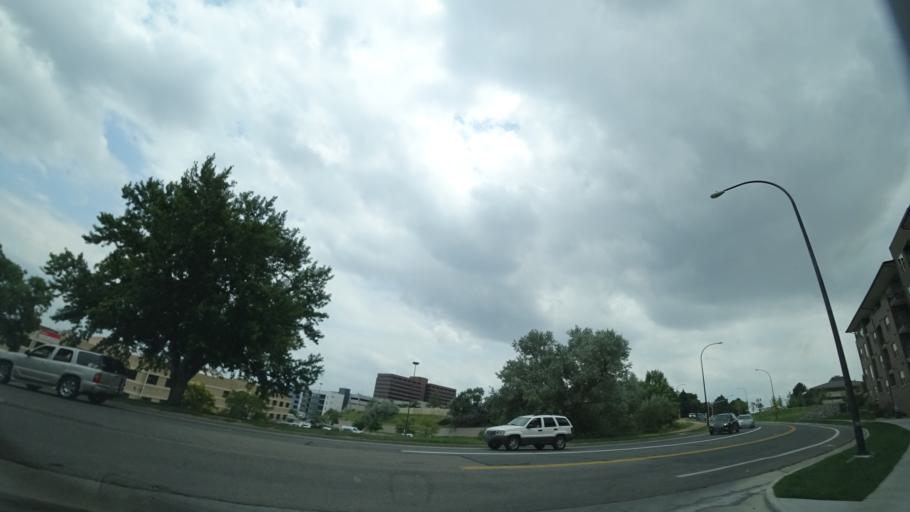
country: US
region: Colorado
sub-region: Jefferson County
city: West Pleasant View
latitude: 39.7155
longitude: -105.1380
